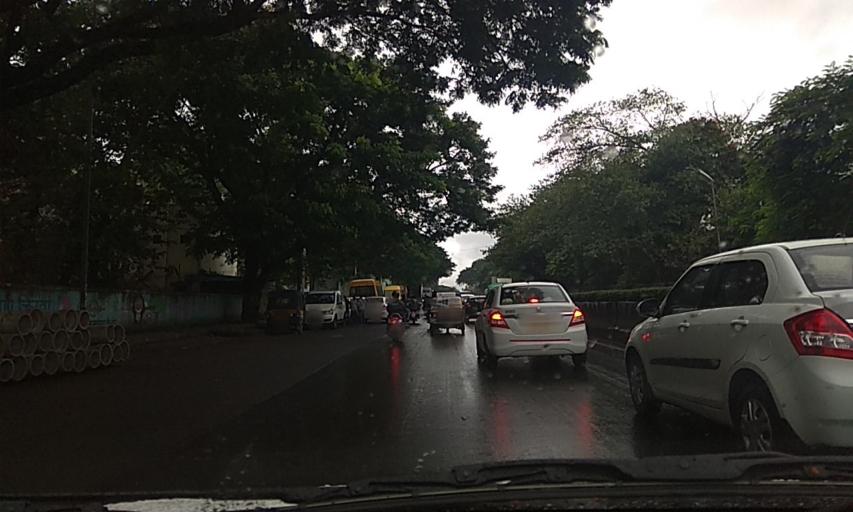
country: IN
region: Maharashtra
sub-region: Pune Division
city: Khadki
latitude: 18.5529
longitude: 73.8871
